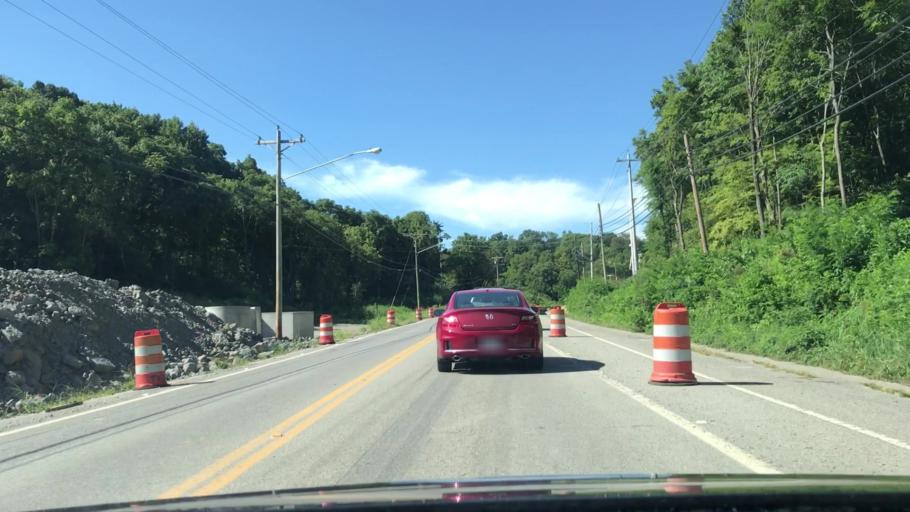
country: US
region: Tennessee
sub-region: Williamson County
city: Brentwood Estates
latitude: 35.9793
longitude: -86.8231
